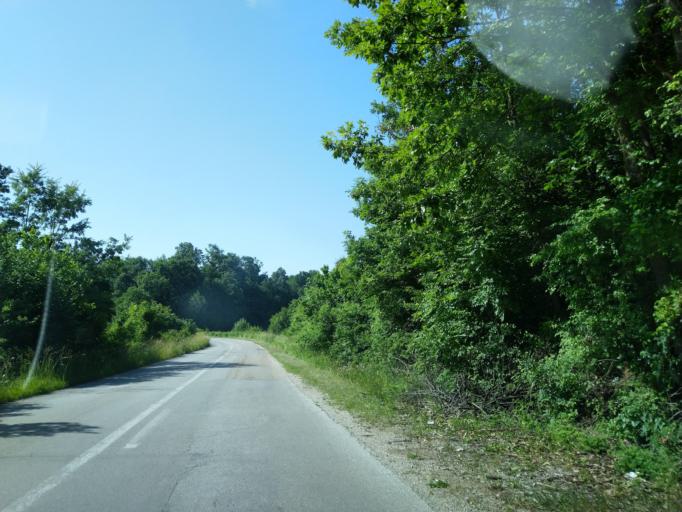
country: RS
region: Central Serbia
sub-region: Zlatiborski Okrug
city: Cajetina
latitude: 43.8628
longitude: 19.7023
